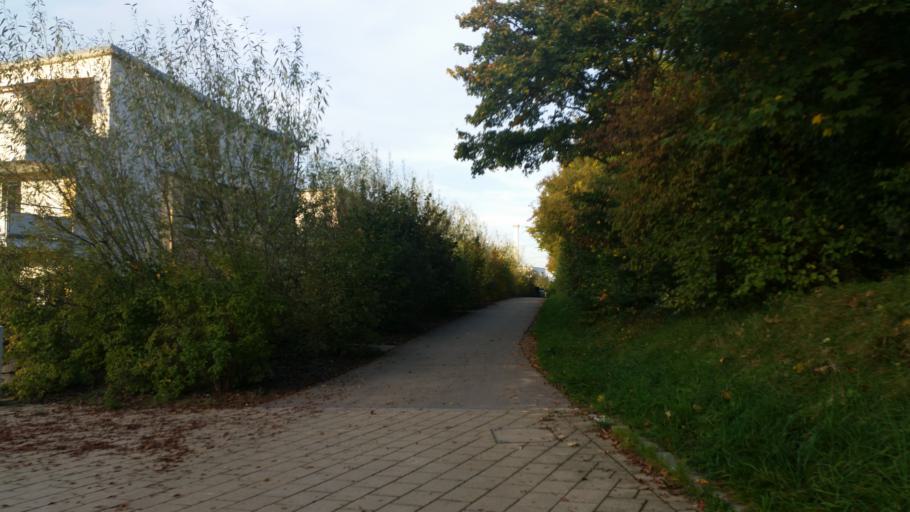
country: DE
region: Baden-Wuerttemberg
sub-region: Regierungsbezirk Stuttgart
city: Freiberg am Neckar
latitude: 48.9190
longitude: 9.2212
